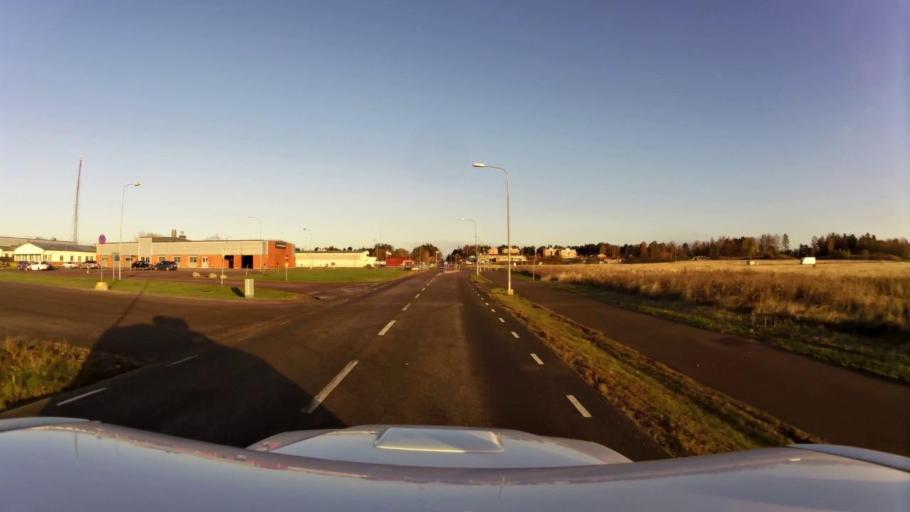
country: SE
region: OEstergoetland
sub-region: Linkopings Kommun
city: Linkoping
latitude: 58.4220
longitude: 15.6792
